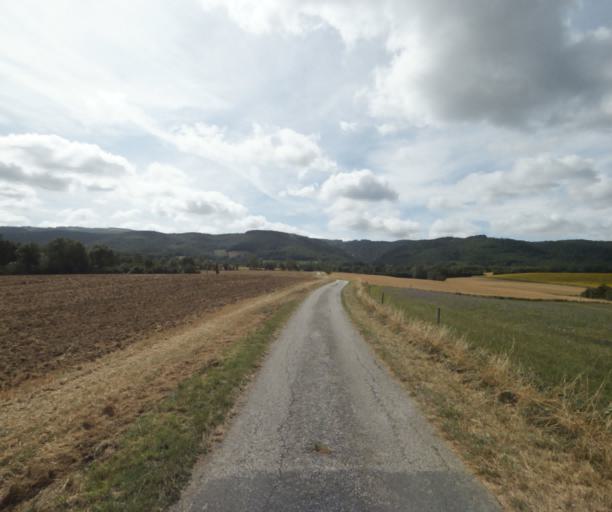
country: FR
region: Midi-Pyrenees
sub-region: Departement du Tarn
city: Soreze
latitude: 43.4752
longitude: 2.0980
